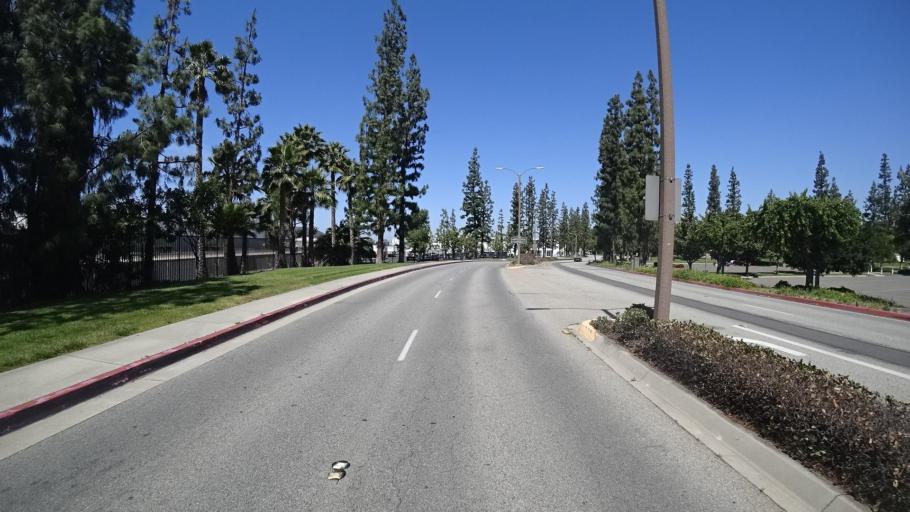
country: US
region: California
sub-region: Los Angeles County
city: La Puente
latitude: 34.0178
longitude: -117.9647
